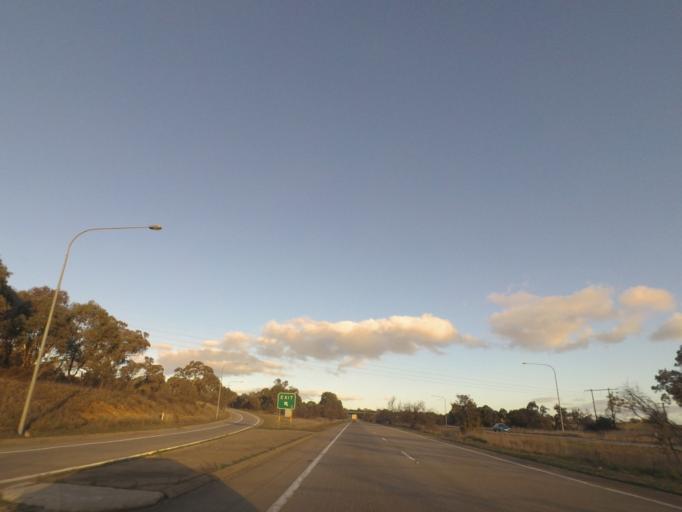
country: AU
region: New South Wales
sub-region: Yass Valley
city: Yass
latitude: -34.7968
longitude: 148.8719
